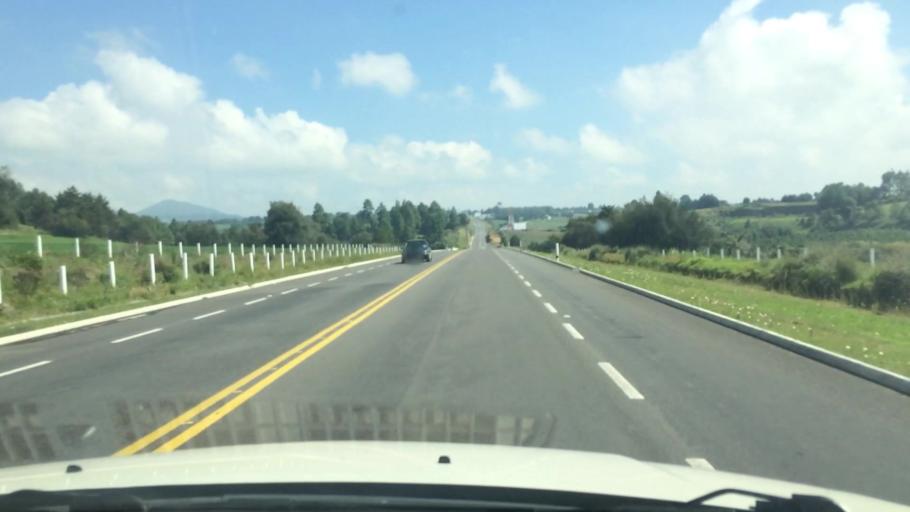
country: MX
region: Mexico
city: Amanalco de Becerra
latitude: 19.3153
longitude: -100.0041
